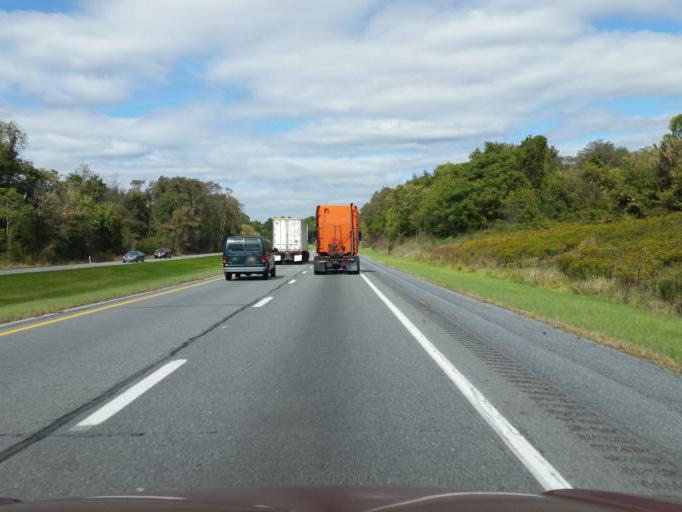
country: US
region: Pennsylvania
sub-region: Dauphin County
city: Middletown
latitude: 40.2166
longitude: -76.7096
